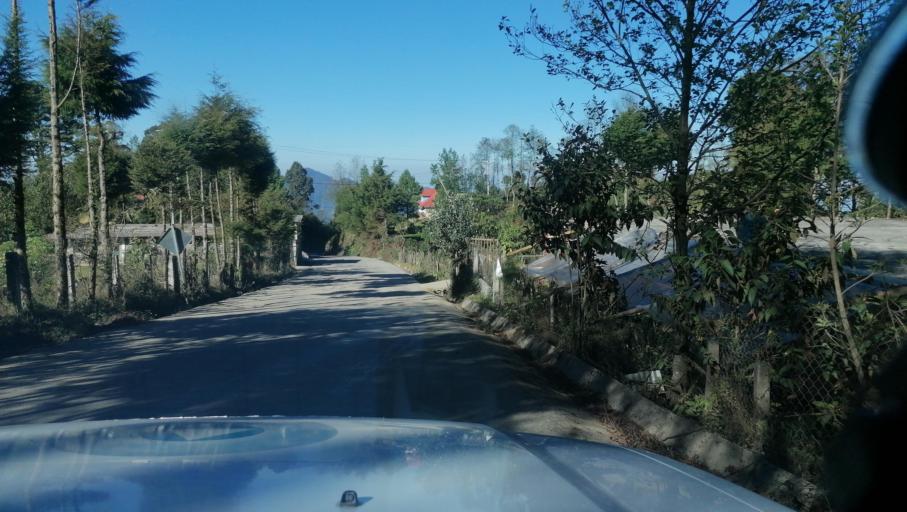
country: MX
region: Chiapas
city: Motozintla de Mendoza
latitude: 15.2738
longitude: -92.2313
